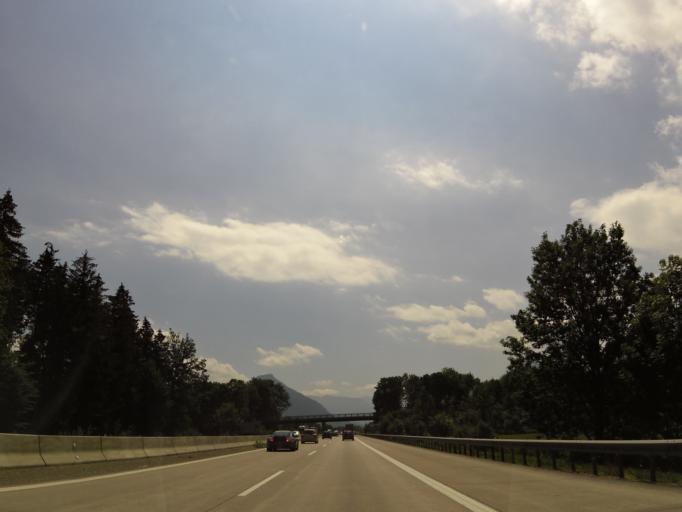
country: DE
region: Bavaria
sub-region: Upper Bavaria
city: Brannenburg
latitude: 47.7516
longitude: 12.1157
